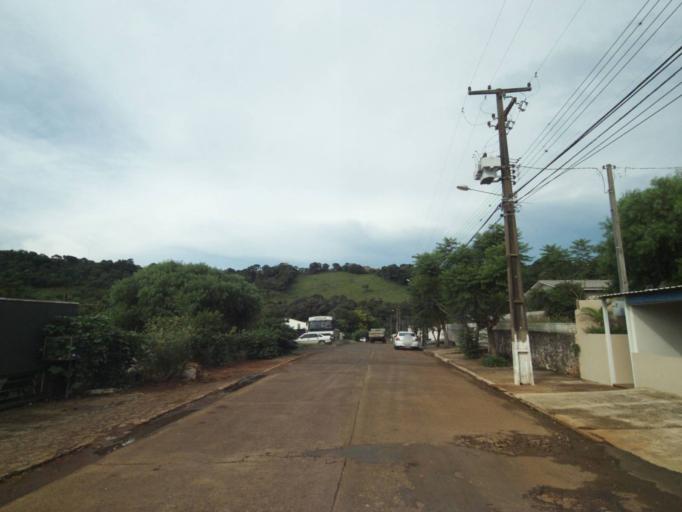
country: BR
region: Parana
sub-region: Guaraniacu
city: Guaraniacu
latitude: -25.1014
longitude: -52.8765
